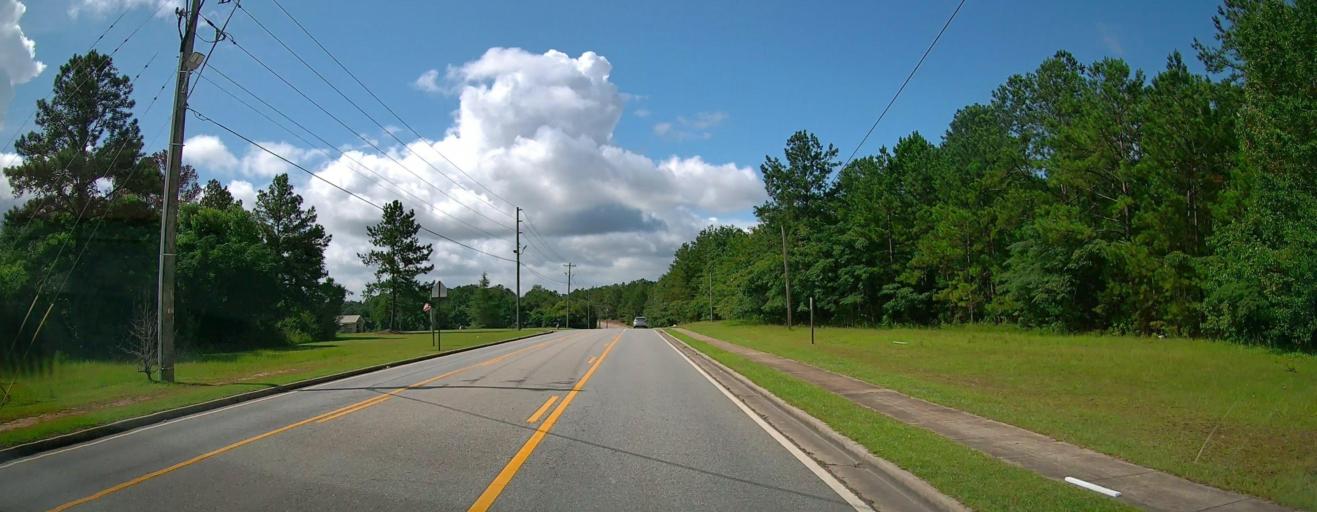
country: US
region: Georgia
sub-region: Houston County
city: Warner Robins
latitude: 32.5921
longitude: -83.6371
